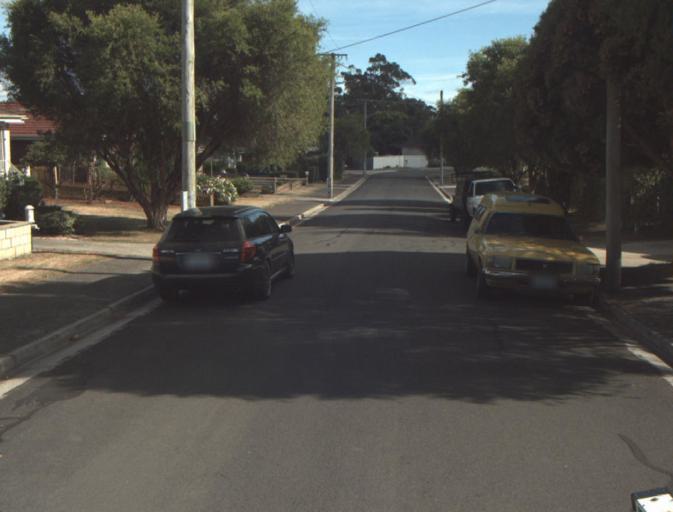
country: AU
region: Tasmania
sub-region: Launceston
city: Newstead
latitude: -41.4608
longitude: 147.1734
